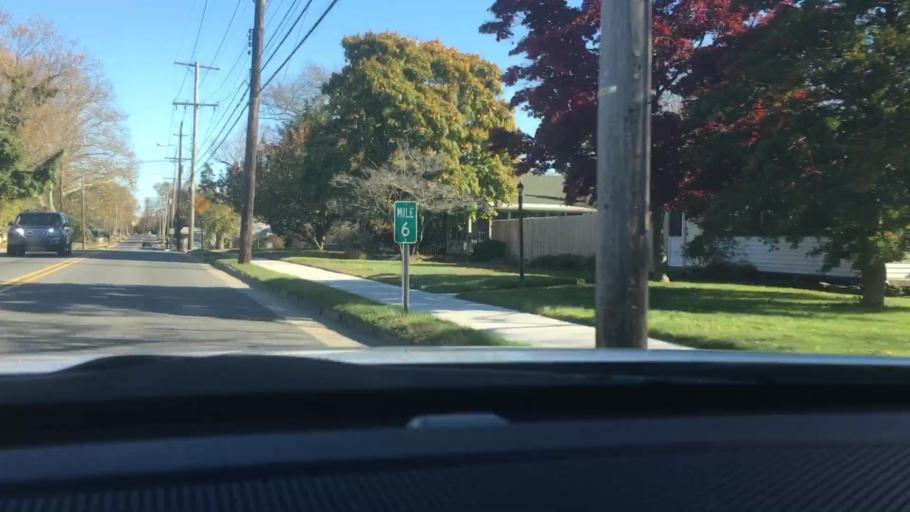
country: US
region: New Jersey
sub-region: Atlantic County
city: Pleasantville
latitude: 39.3791
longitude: -74.5345
